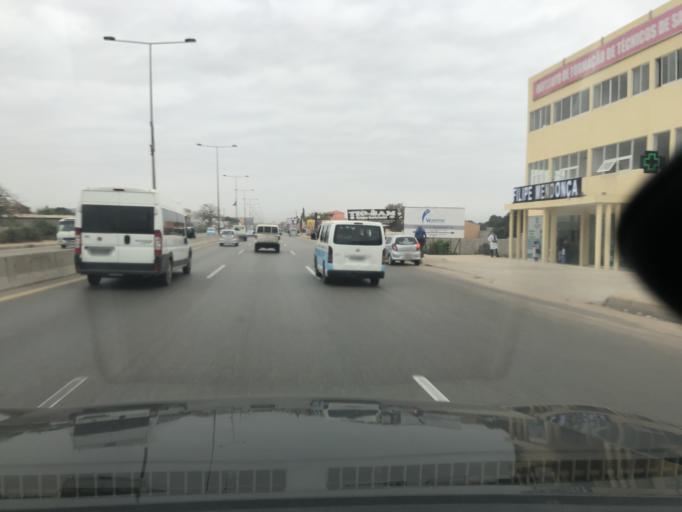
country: AO
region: Luanda
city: Luanda
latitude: -8.9676
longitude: 13.1602
